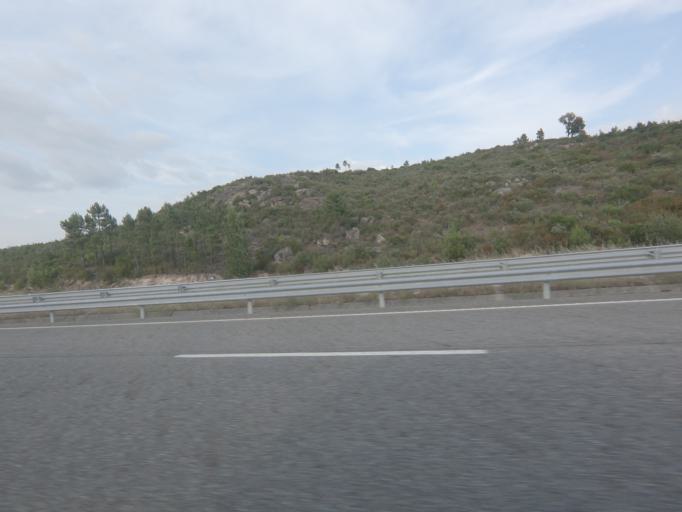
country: PT
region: Vila Real
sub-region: Boticas
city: Boticas
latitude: 41.6331
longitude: -7.5955
